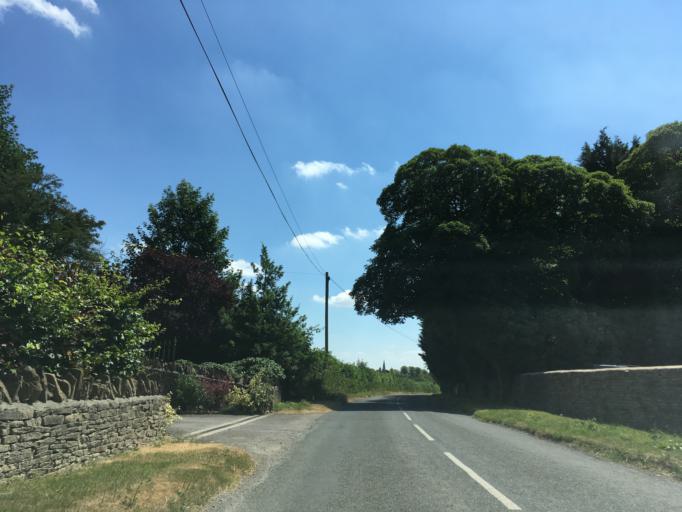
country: GB
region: England
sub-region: Gloucestershire
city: Chalford
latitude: 51.7573
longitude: -2.1461
